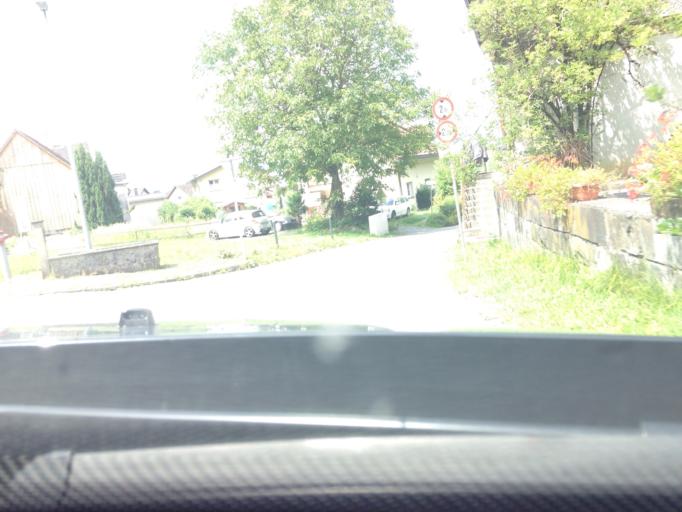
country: AT
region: Vorarlberg
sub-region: Politischer Bezirk Dornbirn
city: Hohenems
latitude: 47.3605
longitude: 9.6918
